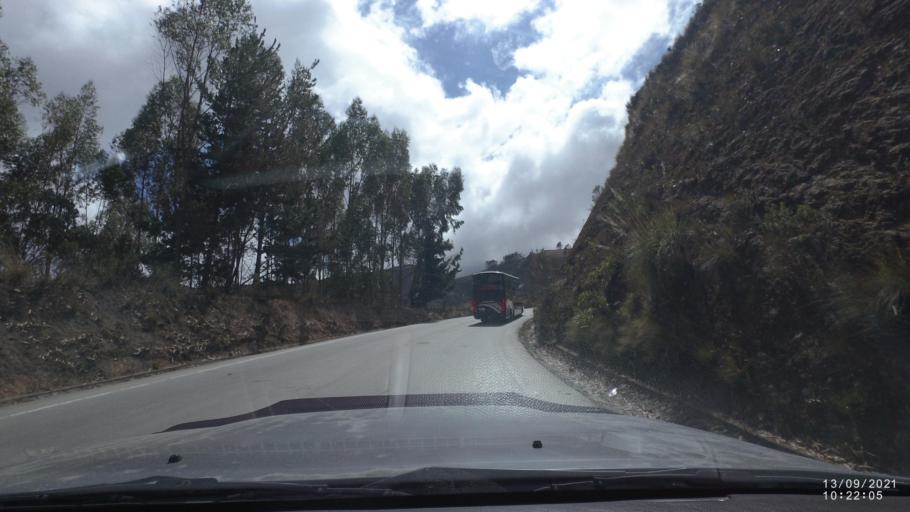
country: BO
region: Cochabamba
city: Colomi
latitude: -17.3174
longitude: -65.8737
